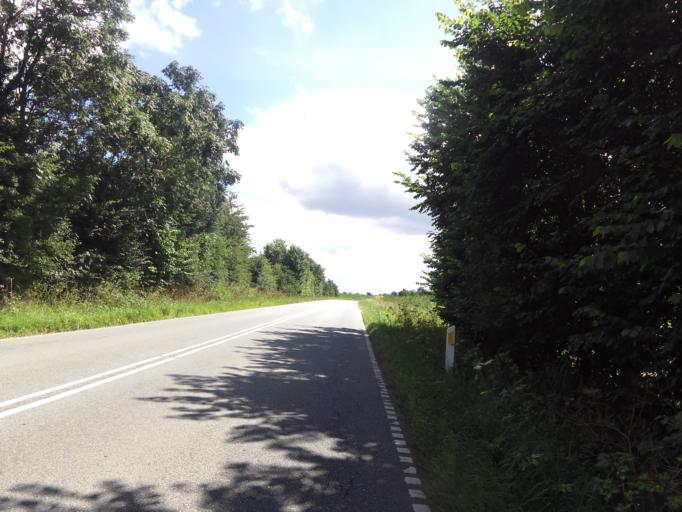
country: DK
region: South Denmark
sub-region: Haderslev Kommune
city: Haderslev
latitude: 55.2630
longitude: 9.4381
